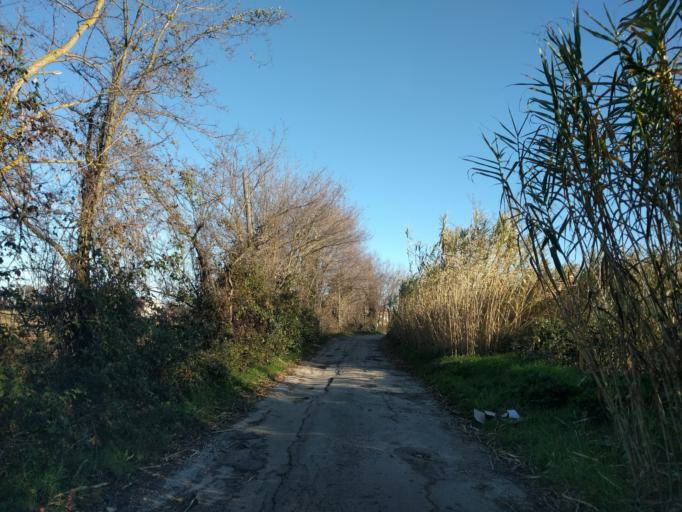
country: IT
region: The Marches
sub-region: Provincia di Pesaro e Urbino
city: Cuccurano
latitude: 43.7972
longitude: 12.9806
